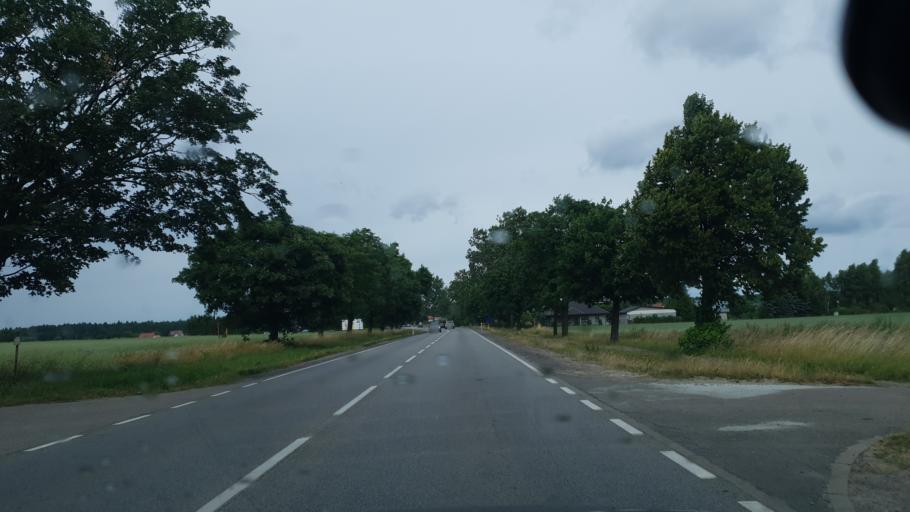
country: PL
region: Pomeranian Voivodeship
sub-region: Powiat kartuski
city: Banino
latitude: 54.4238
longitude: 18.3841
